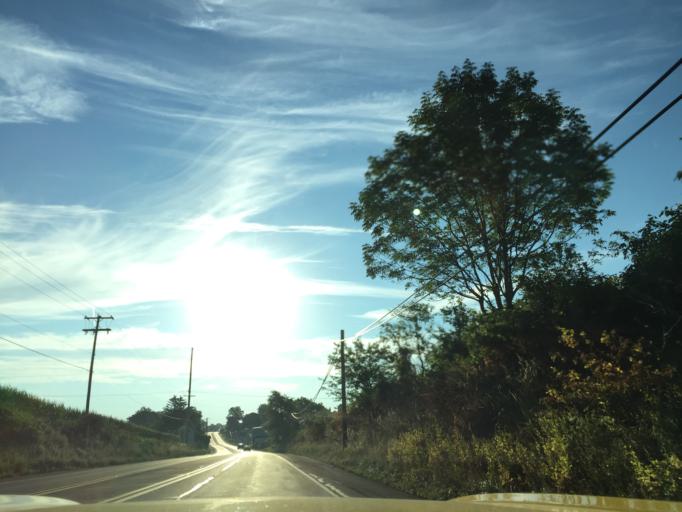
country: US
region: Pennsylvania
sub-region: Berks County
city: Kutztown
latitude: 40.5333
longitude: -75.7478
